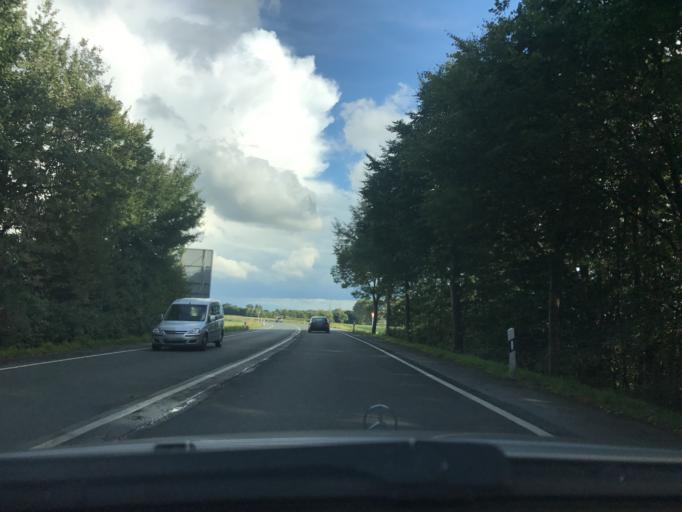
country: DE
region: North Rhine-Westphalia
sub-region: Regierungsbezirk Arnsberg
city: Welver
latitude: 51.6930
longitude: 7.9734
